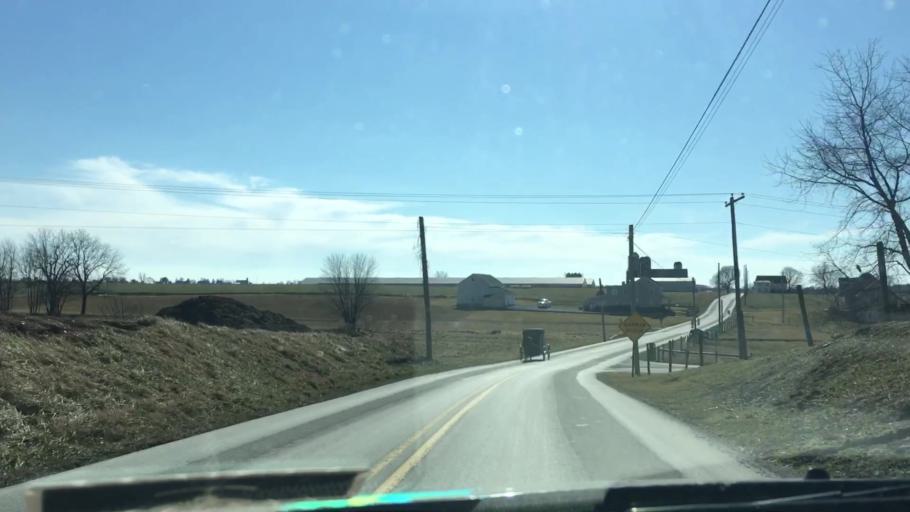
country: US
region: Pennsylvania
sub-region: Lancaster County
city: New Holland
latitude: 40.1181
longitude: -76.1312
